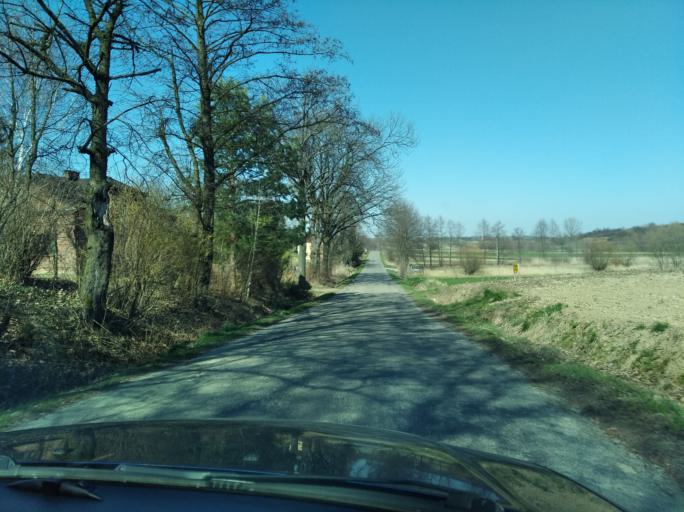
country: PL
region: Subcarpathian Voivodeship
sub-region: Powiat przeworski
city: Pantalowice
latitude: 49.9362
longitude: 22.4454
